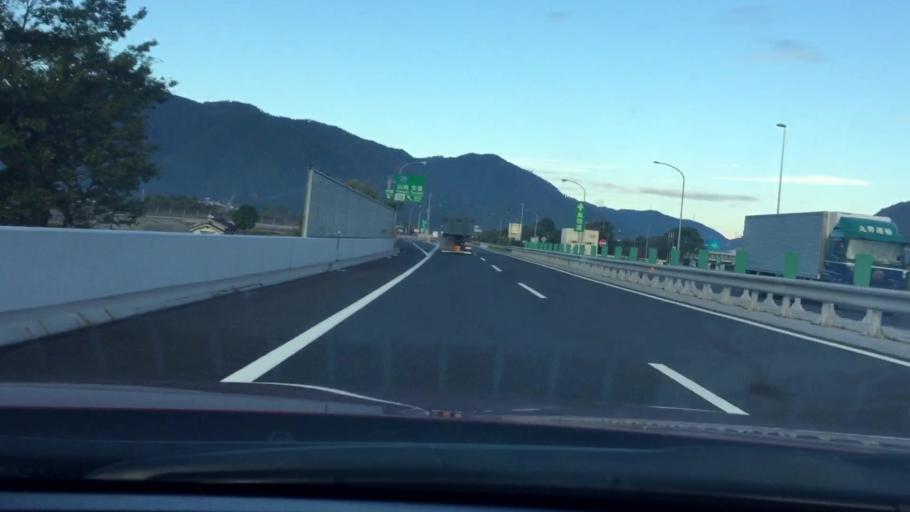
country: JP
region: Hyogo
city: Yamazakicho-nakabirose
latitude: 34.9984
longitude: 134.5525
